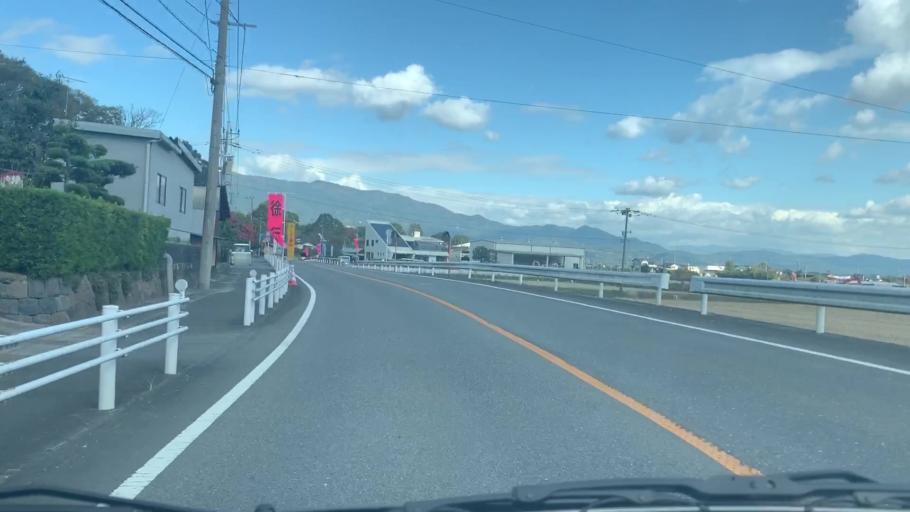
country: JP
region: Saga Prefecture
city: Saga-shi
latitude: 33.2686
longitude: 130.1804
